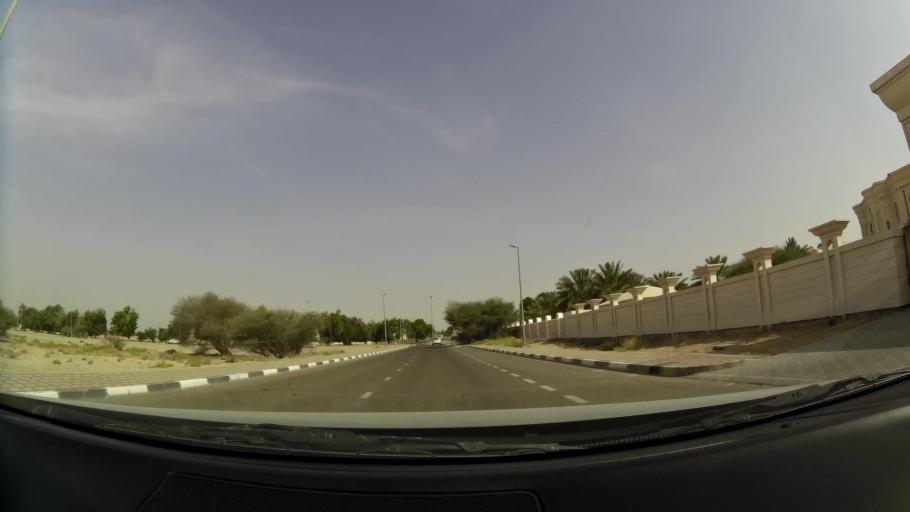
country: AE
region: Abu Dhabi
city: Al Ain
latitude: 24.1612
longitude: 55.7068
